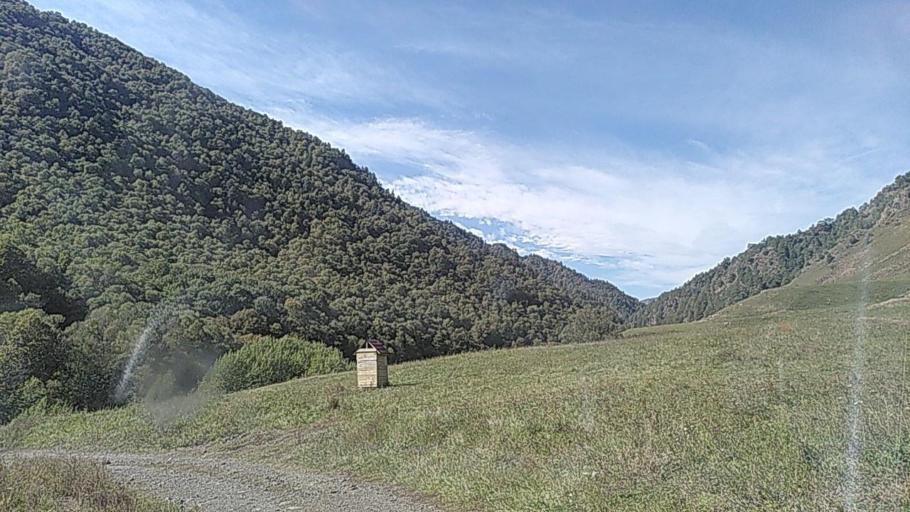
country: RU
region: Kabardino-Balkariya
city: Kamennomostskoye
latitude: 43.7174
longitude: 42.8367
